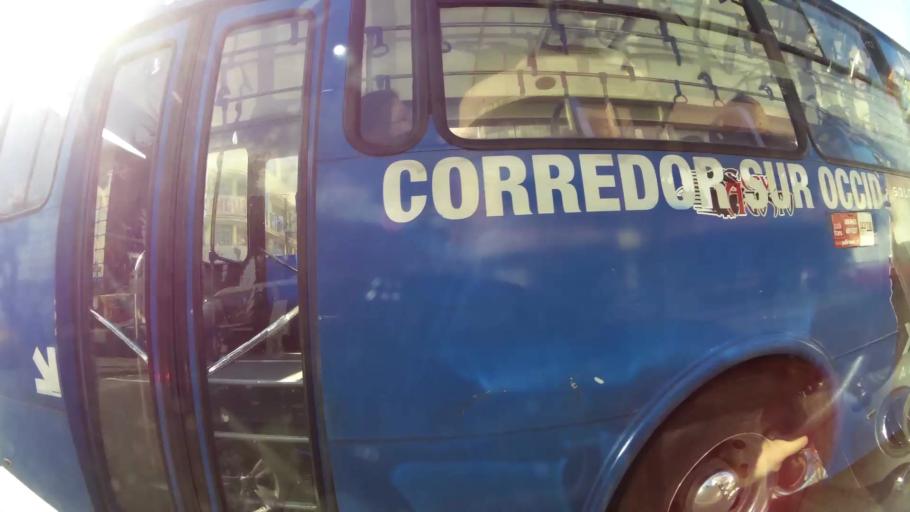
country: EC
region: Pichincha
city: Quito
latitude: -0.2403
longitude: -78.5314
